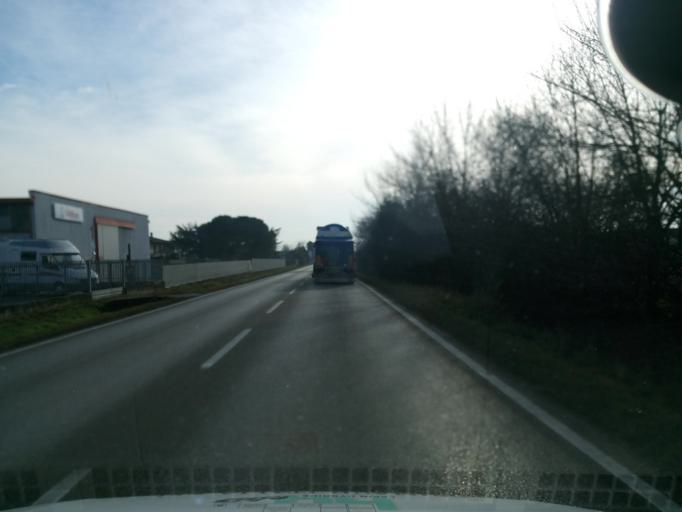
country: IT
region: Veneto
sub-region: Provincia di Vicenza
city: Sandrigo
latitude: 45.6617
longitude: 11.5799
